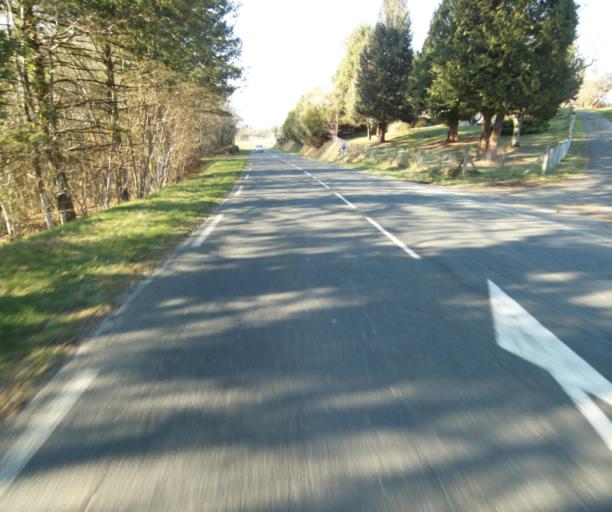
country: FR
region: Limousin
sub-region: Departement de la Correze
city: Saint-Clement
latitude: 45.3178
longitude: 1.6798
